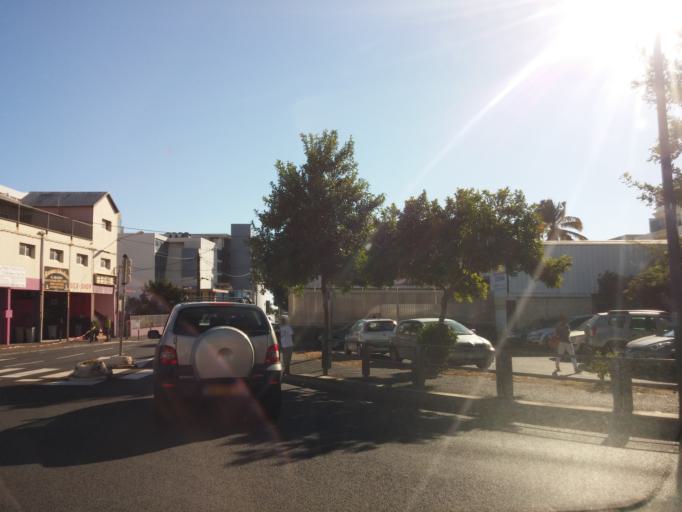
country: RE
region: Reunion
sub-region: Reunion
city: Saint-Denis
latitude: -20.8817
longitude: 55.4596
